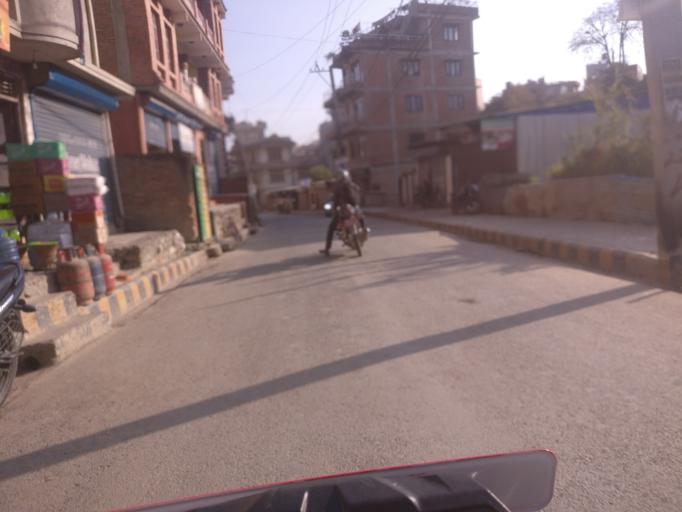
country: NP
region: Central Region
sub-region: Bagmati Zone
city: Patan
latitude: 27.6602
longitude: 85.3294
